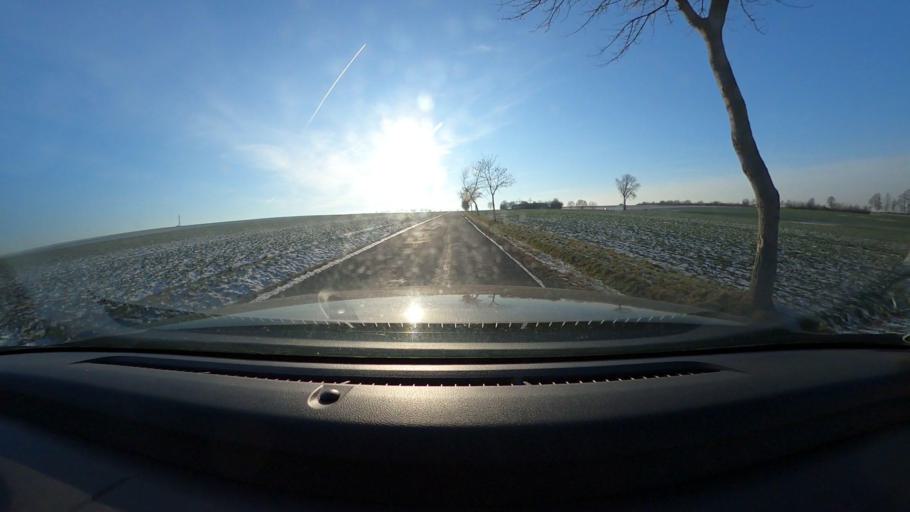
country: DE
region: Saxony
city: Grossschirma
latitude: 50.9523
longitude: 13.2323
